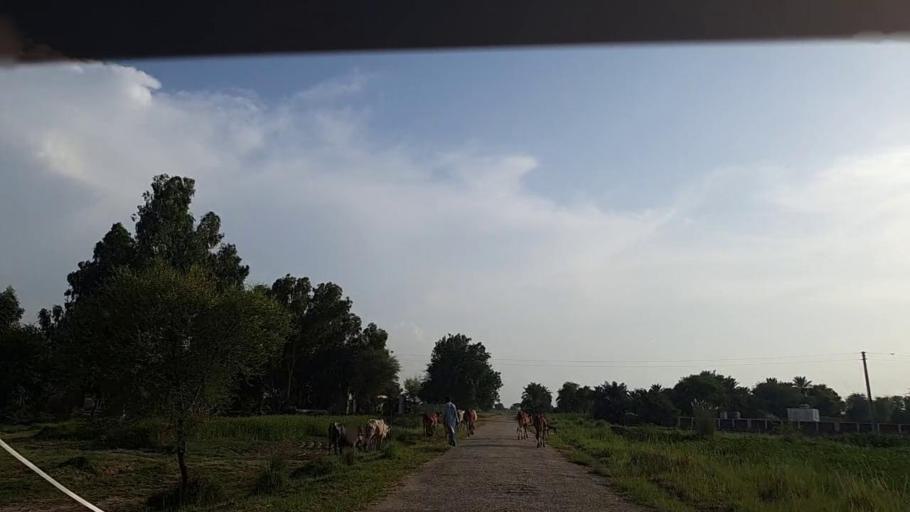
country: PK
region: Sindh
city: Khanpur
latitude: 27.8189
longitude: 69.3383
